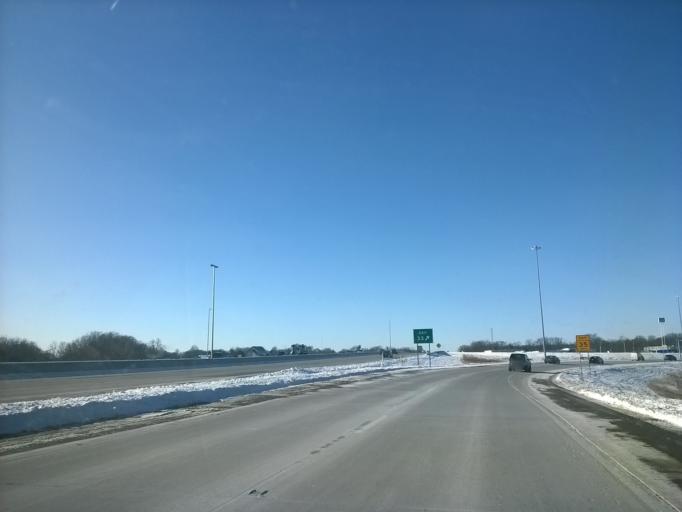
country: US
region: Indiana
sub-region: Marion County
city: Meridian Hills
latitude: 39.9205
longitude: -86.1081
